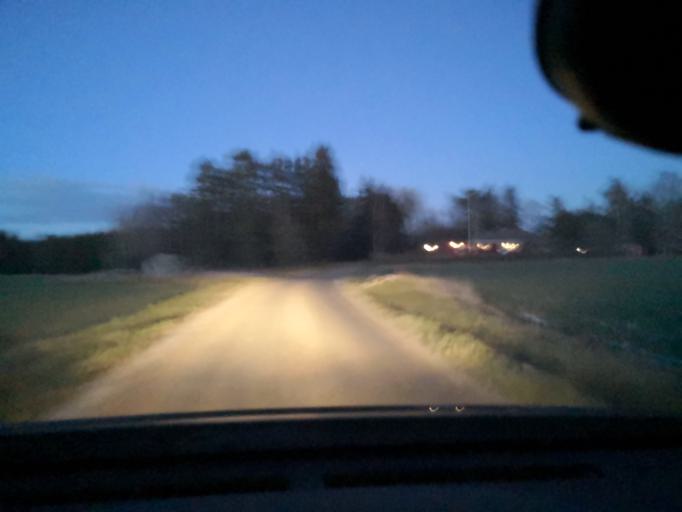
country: SE
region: Vaestmanland
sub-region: Sala Kommun
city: Sala
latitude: 59.8759
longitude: 16.7275
